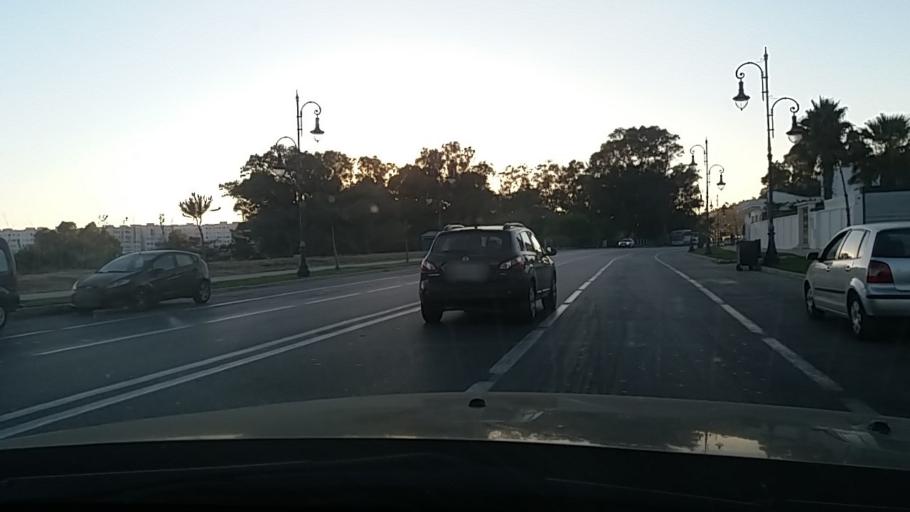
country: MA
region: Tanger-Tetouan
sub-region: Tanger-Assilah
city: Boukhalef
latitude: 35.7410
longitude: -5.8792
